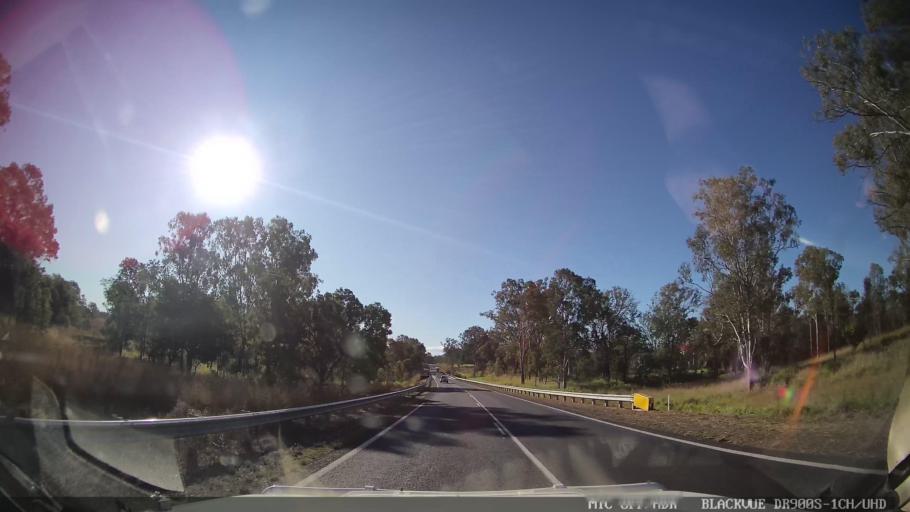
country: AU
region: Queensland
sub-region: Bundaberg
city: Sharon
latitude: -24.8297
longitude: 151.7085
